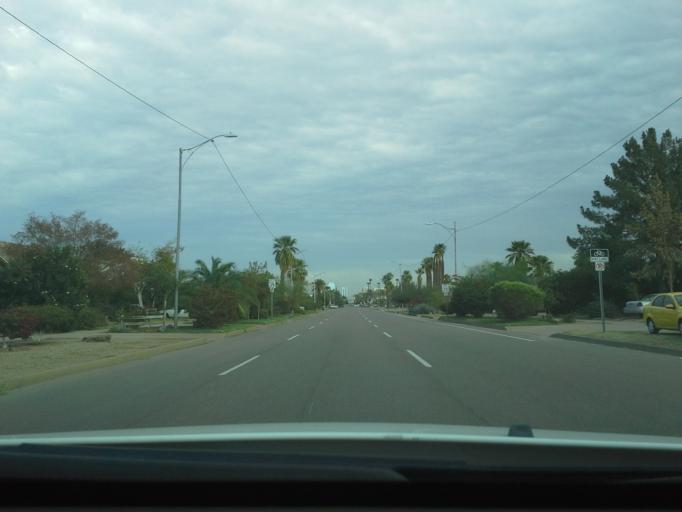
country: US
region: Arizona
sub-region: Maricopa County
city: Phoenix
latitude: 33.4470
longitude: -112.1066
